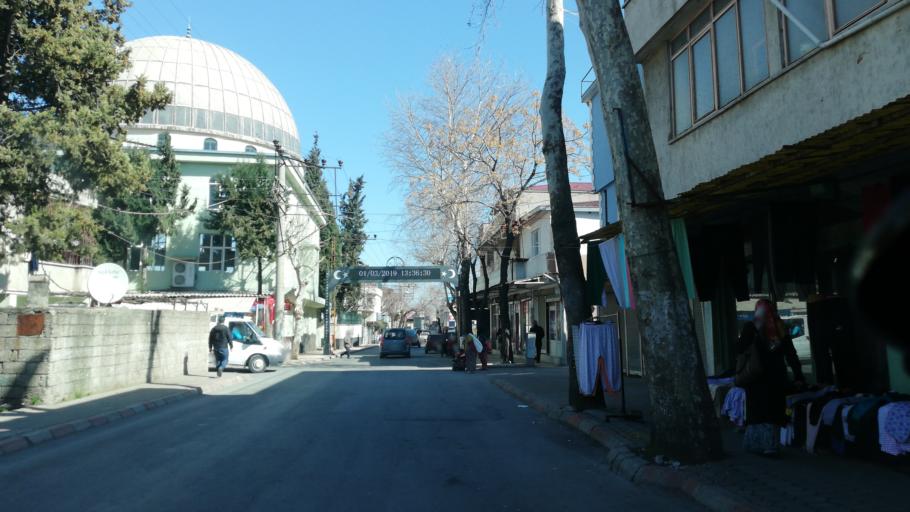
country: TR
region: Kahramanmaras
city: Kahramanmaras
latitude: 37.5748
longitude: 36.9461
